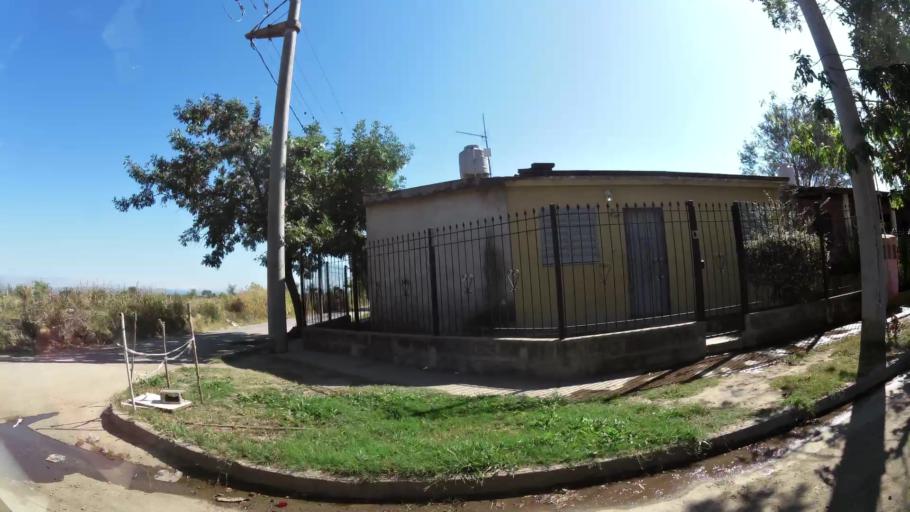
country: AR
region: Cordoba
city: Villa Allende
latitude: -31.3206
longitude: -64.2520
